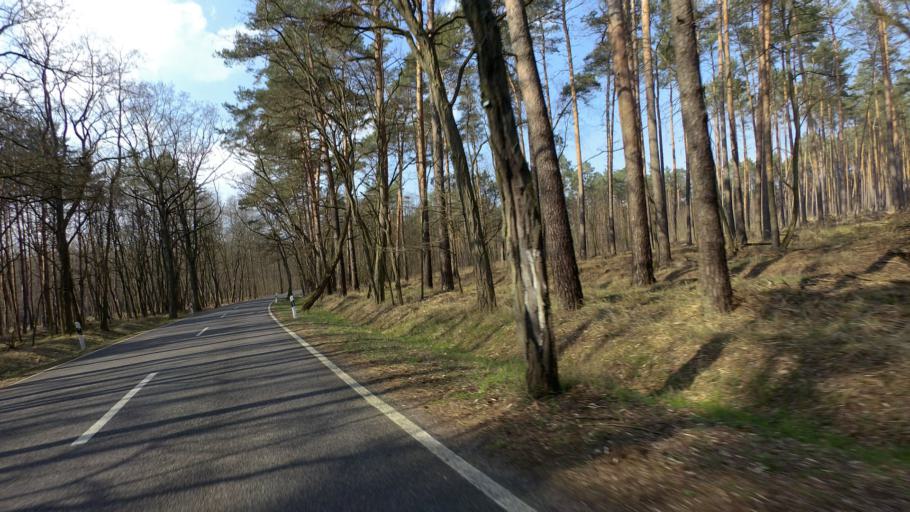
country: DE
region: Brandenburg
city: Dahme
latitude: 51.9298
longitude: 13.4562
